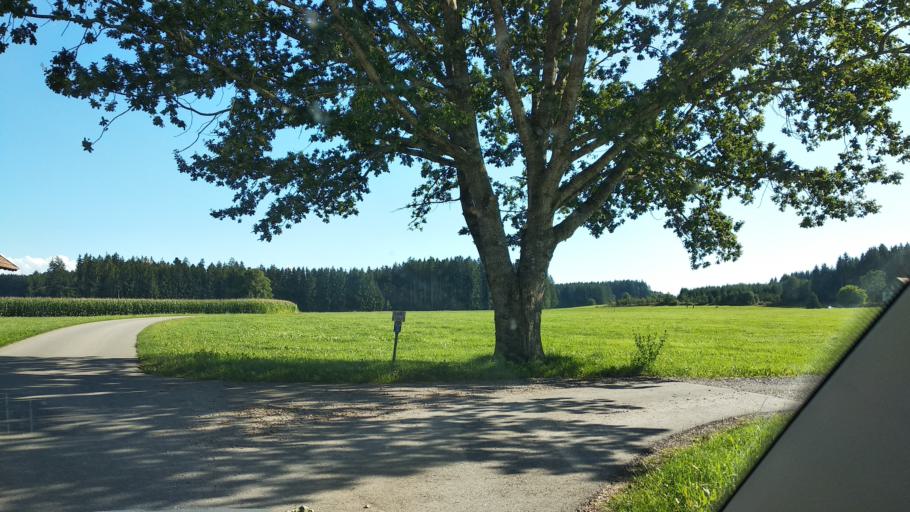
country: DE
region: Baden-Wuerttemberg
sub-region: Tuebingen Region
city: Leutkirch im Allgau
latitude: 47.8085
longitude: 10.0639
